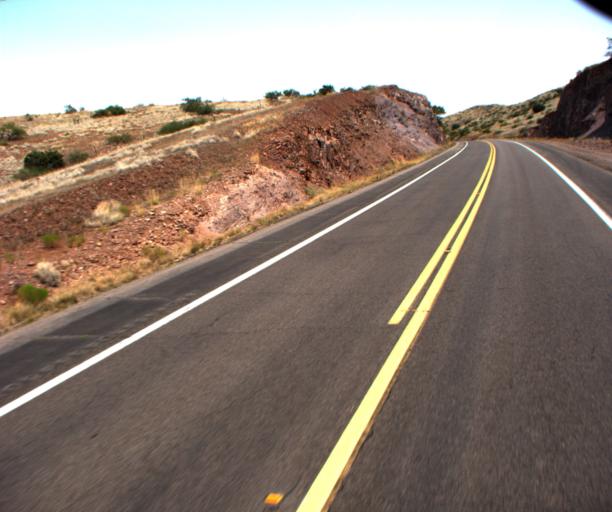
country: US
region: Arizona
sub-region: Greenlee County
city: Clifton
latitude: 32.7535
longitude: -109.2393
